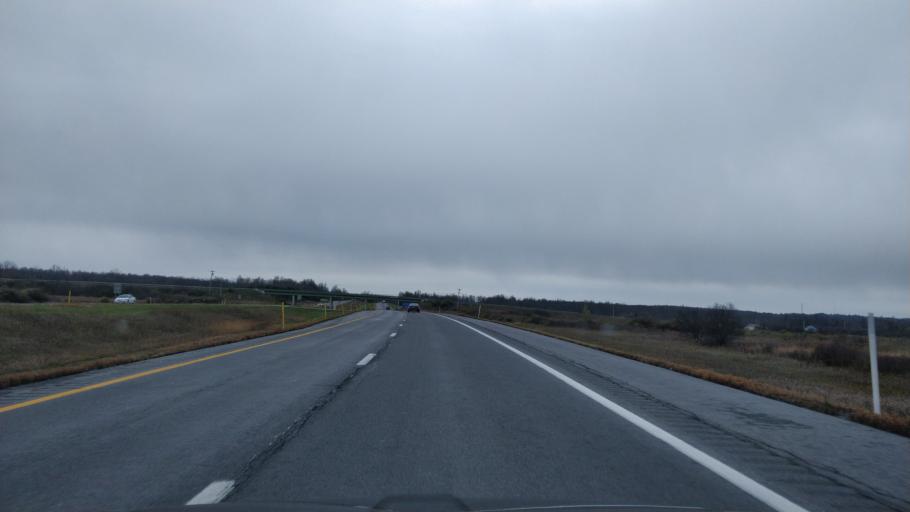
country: US
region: New York
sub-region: Jefferson County
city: Calcium
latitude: 44.0918
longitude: -75.9145
